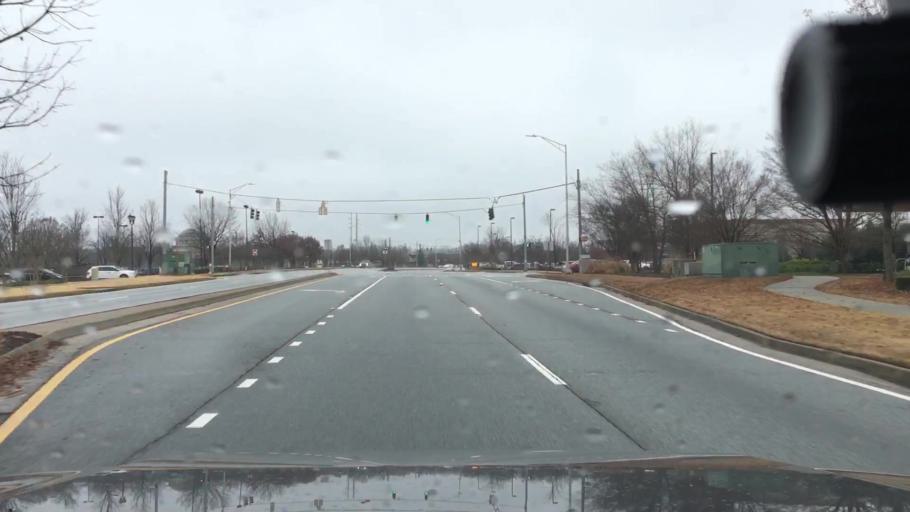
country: US
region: Georgia
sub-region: Coweta County
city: Newnan
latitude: 33.3888
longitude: -84.7625
